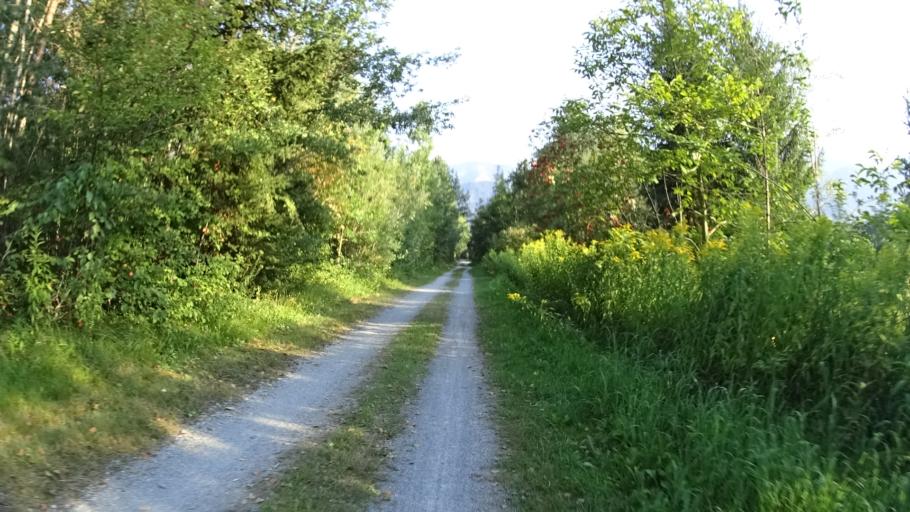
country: AT
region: Carinthia
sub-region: Politischer Bezirk Villach Land
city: Sankt Jakob
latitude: 46.5443
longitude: 14.0886
